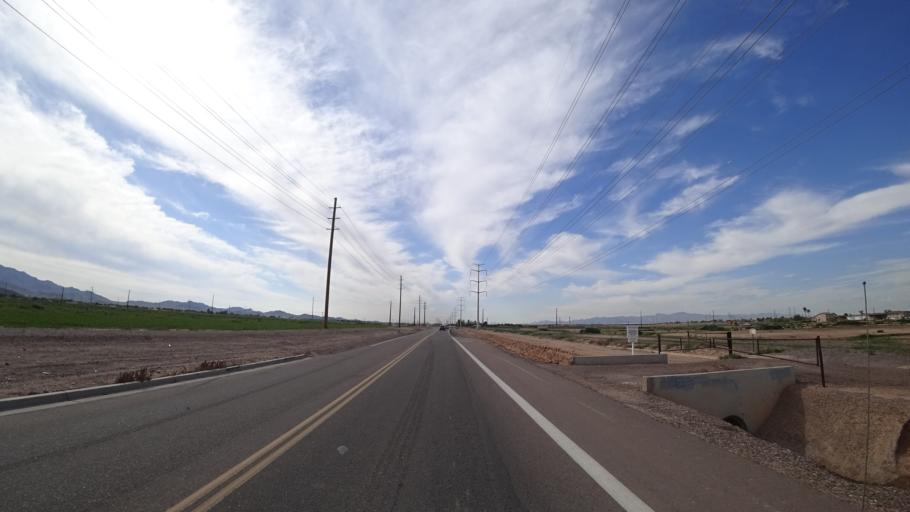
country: US
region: Arizona
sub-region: Maricopa County
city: Tolleson
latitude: 33.4065
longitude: -112.2855
